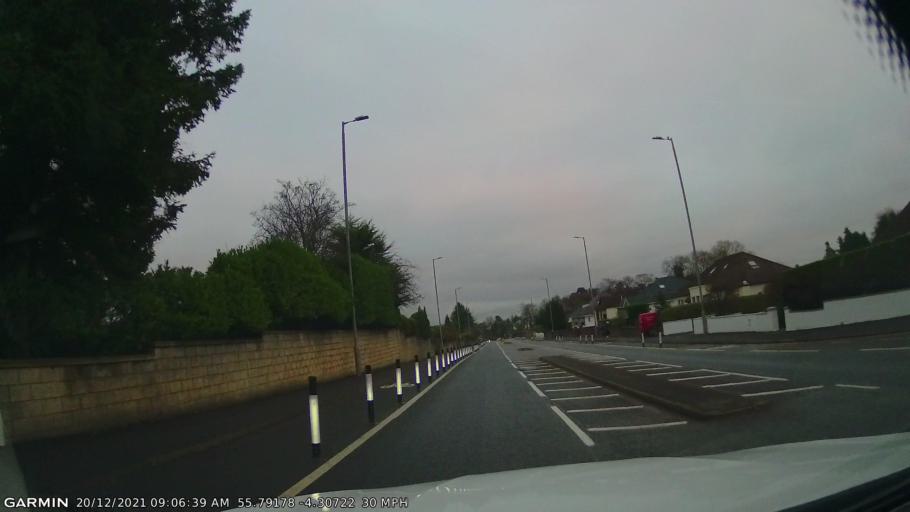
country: GB
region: Scotland
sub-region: East Renfrewshire
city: Giffnock
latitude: 55.7918
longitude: -4.3072
